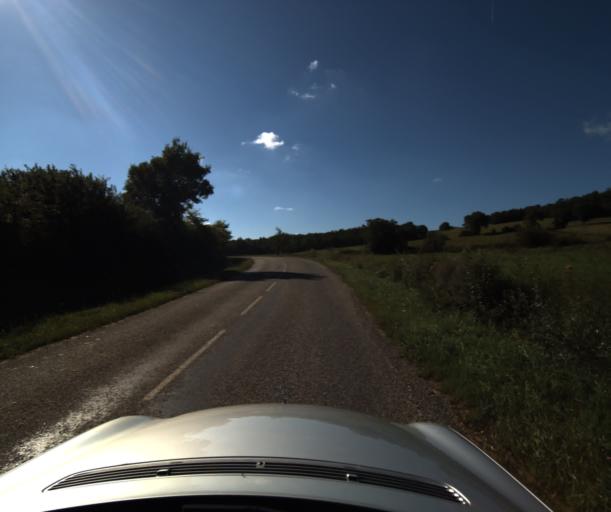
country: FR
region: Midi-Pyrenees
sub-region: Departement de l'Ariege
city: Belesta
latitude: 42.9738
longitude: 1.9219
